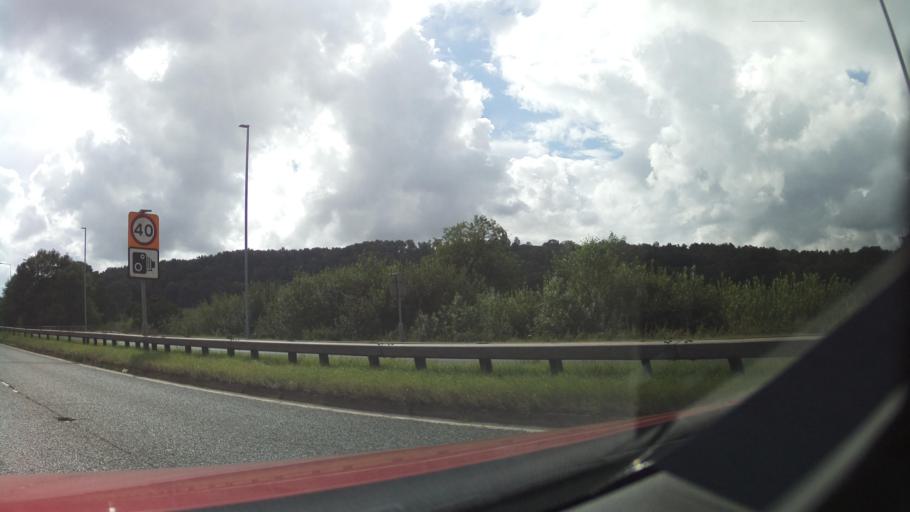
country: GB
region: England
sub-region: Staffordshire
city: Barlaston
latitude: 52.9511
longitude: -2.1912
